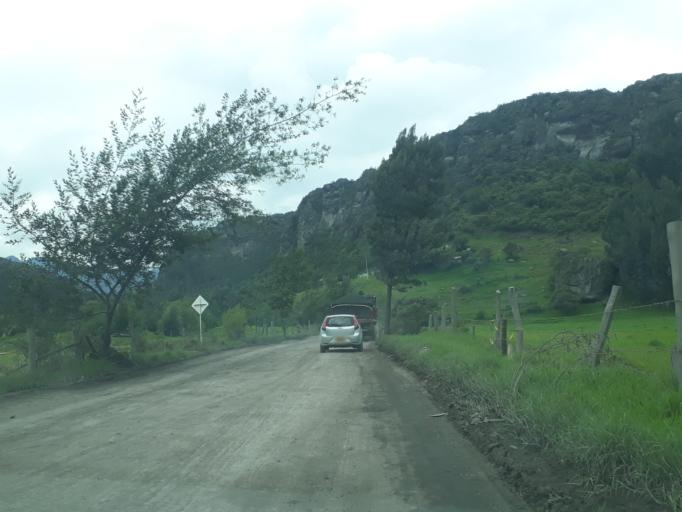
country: CO
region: Cundinamarca
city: Lenguazaque
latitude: 5.3276
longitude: -73.7059
